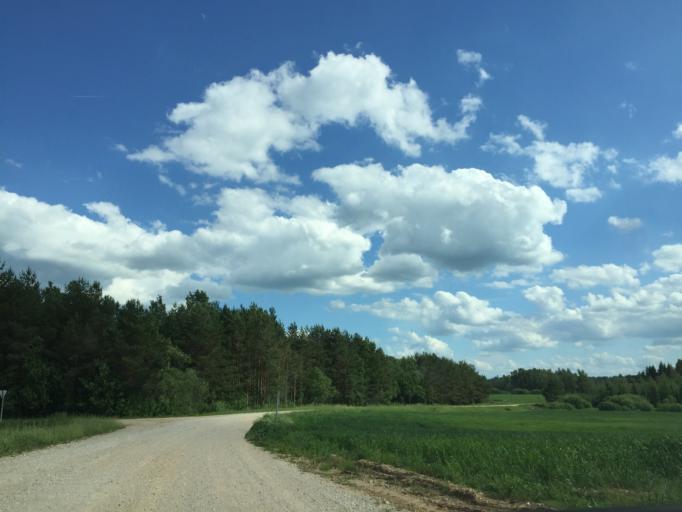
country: LV
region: Jaunpils
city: Jaunpils
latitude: 56.8119
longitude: 23.0770
